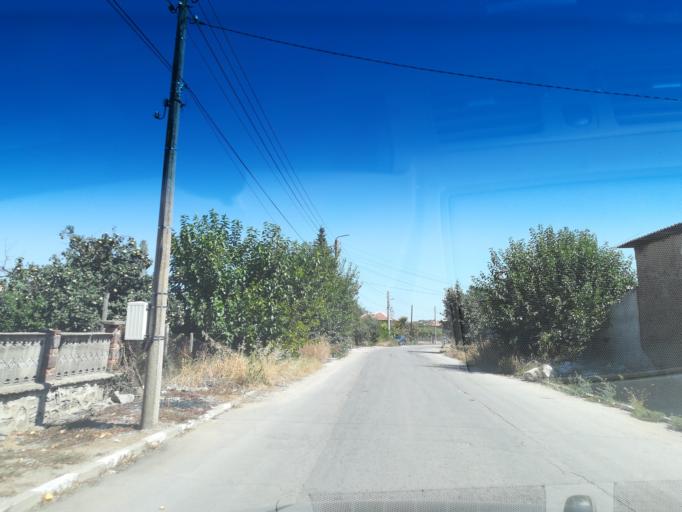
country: BG
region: Pazardzhik
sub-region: Obshtina Pazardzhik
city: Pazardzhik
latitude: 42.2515
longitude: 24.4295
